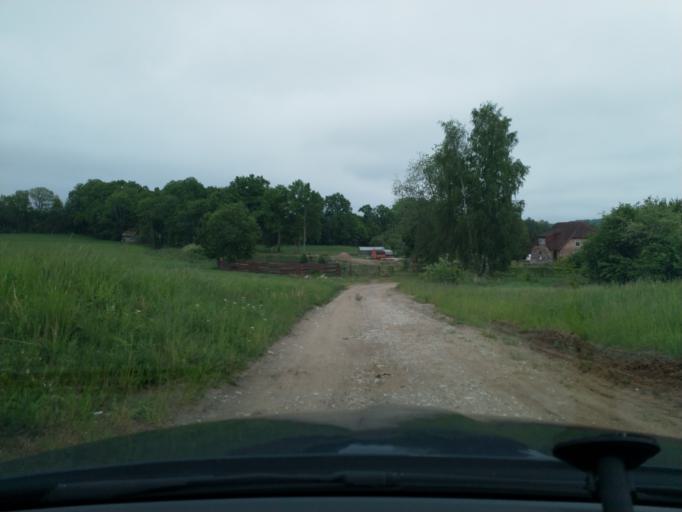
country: LV
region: Kuldigas Rajons
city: Kuldiga
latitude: 56.8773
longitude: 21.8261
